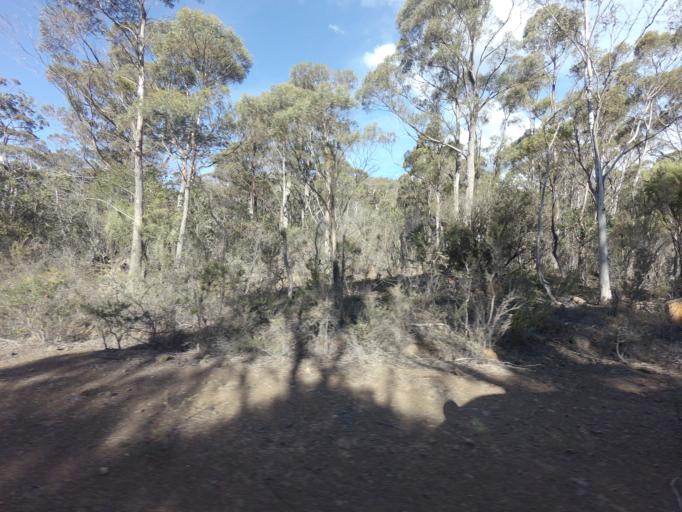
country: AU
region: Tasmania
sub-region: Break O'Day
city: St Helens
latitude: -41.8601
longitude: 148.0238
